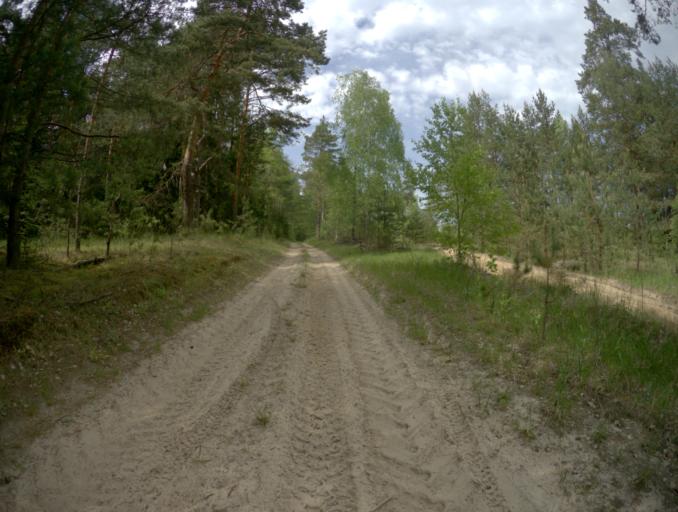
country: RU
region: Vladimir
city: Ivanishchi
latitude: 55.7031
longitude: 40.4646
